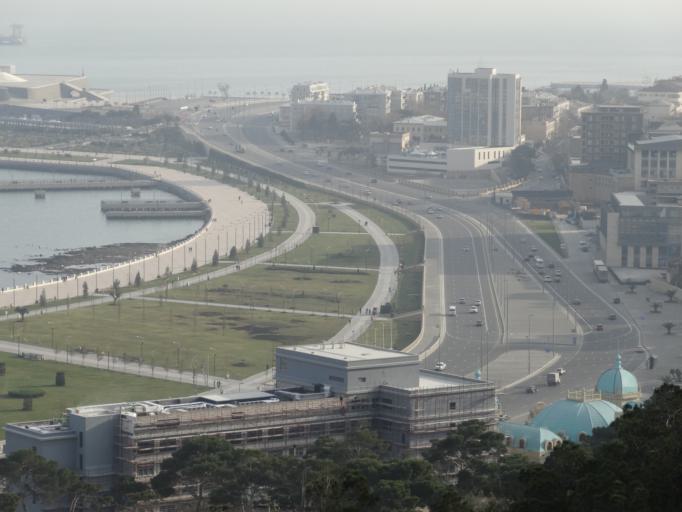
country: AZ
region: Baki
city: Badamdar
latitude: 40.3576
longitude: 49.8304
